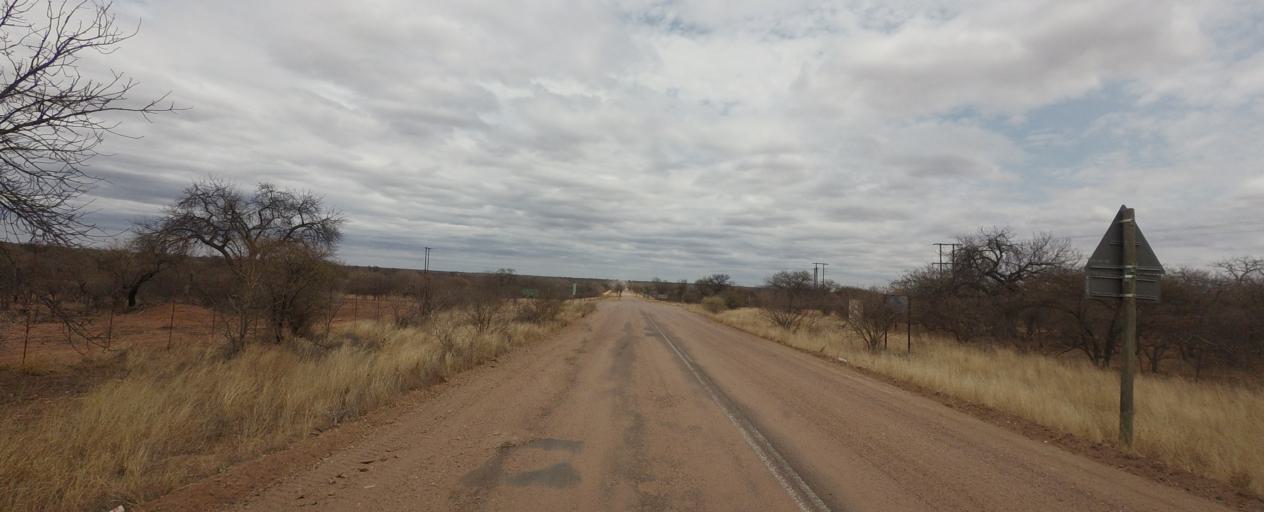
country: BW
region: Central
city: Mathathane
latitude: -22.6813
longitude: 28.6584
